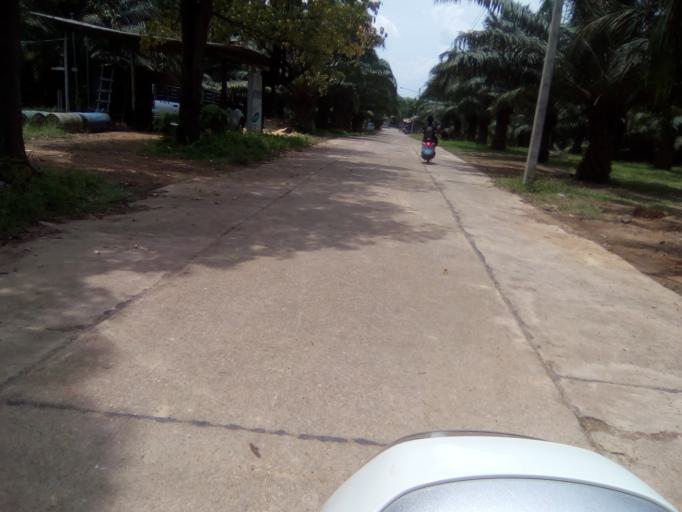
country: TH
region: Krabi
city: Ko Lanta
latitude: 7.5319
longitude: 99.0908
